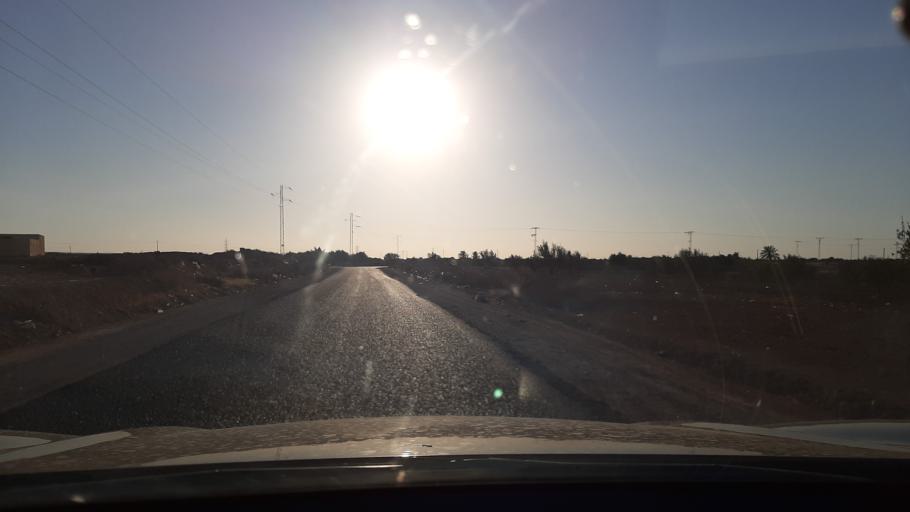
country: TN
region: Qabis
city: Matmata
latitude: 33.6162
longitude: 10.2468
